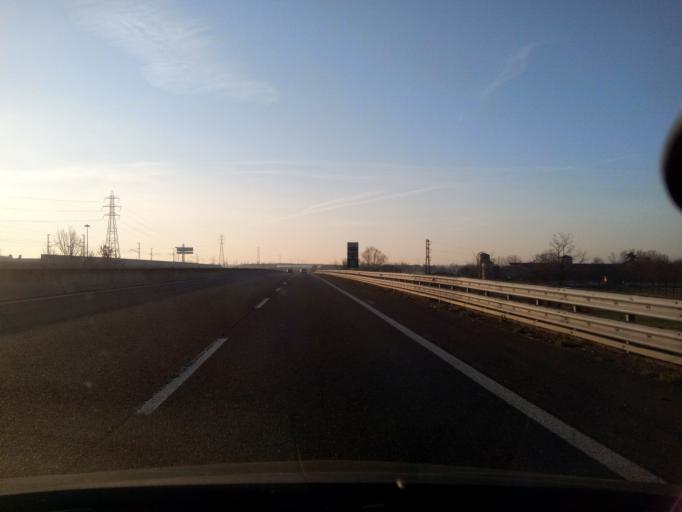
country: IT
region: Lombardy
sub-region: Provincia di Lodi
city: Ospedaletto Lodigiano
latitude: 45.1711
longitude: 9.5932
